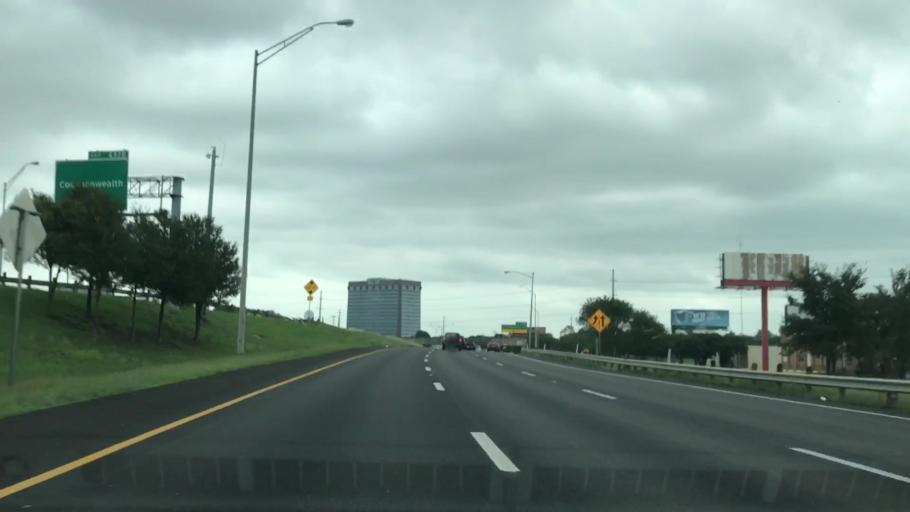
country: US
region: Texas
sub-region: Dallas County
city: Dallas
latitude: 32.8158
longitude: -96.8684
